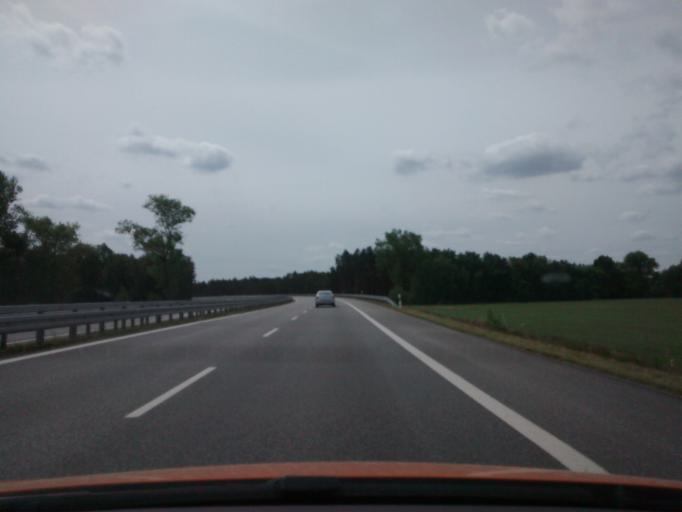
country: DE
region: Brandenburg
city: Trebbin
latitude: 52.1672
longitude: 13.2410
